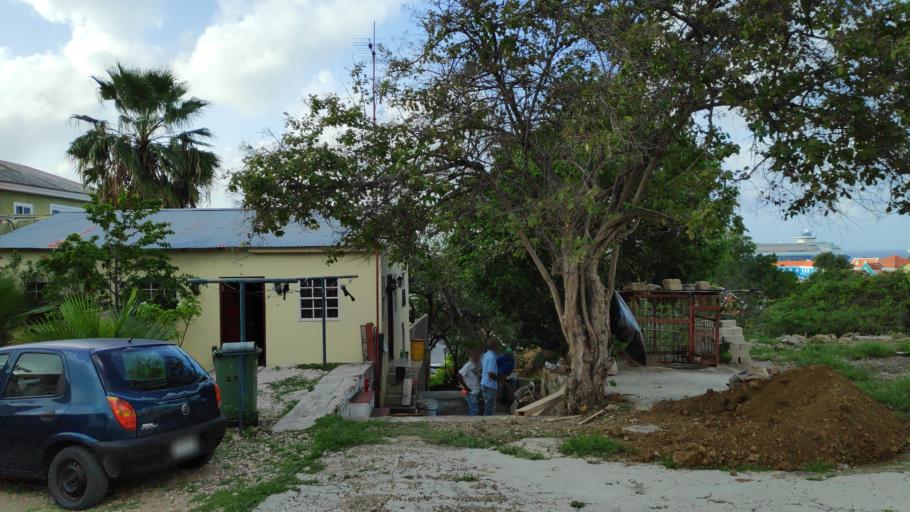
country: CW
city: Willemstad
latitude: 12.1117
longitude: -68.9348
